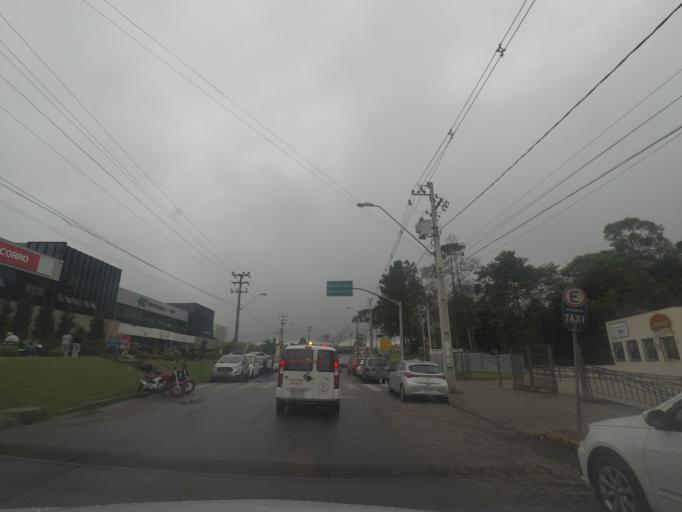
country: BR
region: Parana
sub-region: Quatro Barras
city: Quatro Barras
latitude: -25.3510
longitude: -49.0831
